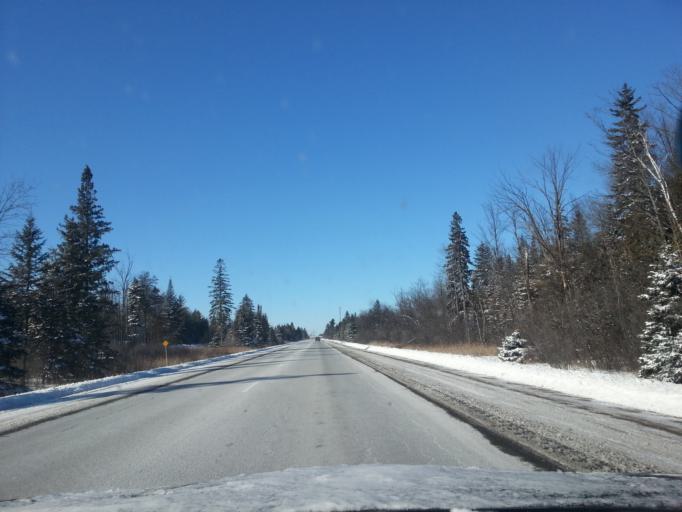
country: CA
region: Ontario
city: Carleton Place
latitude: 45.3181
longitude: -76.0829
